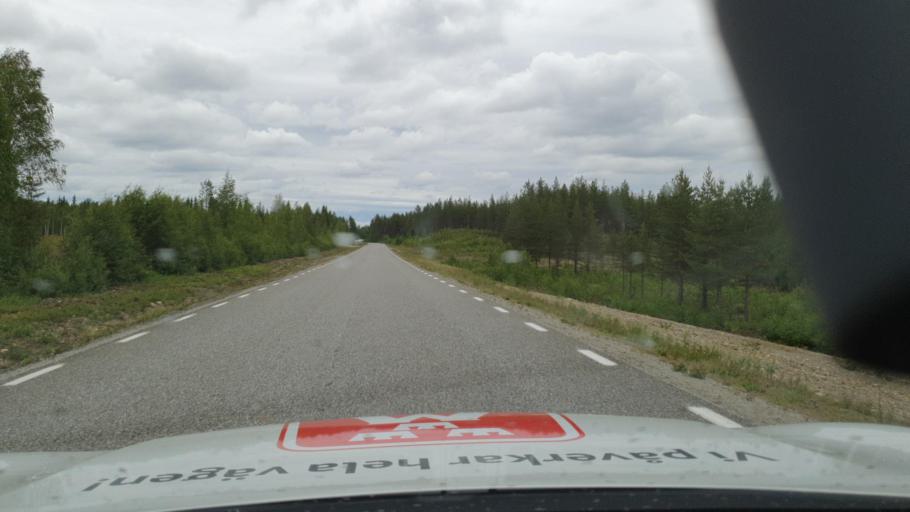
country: SE
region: Vaesterbotten
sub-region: Lycksele Kommun
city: Lycksele
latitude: 64.2198
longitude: 18.2544
